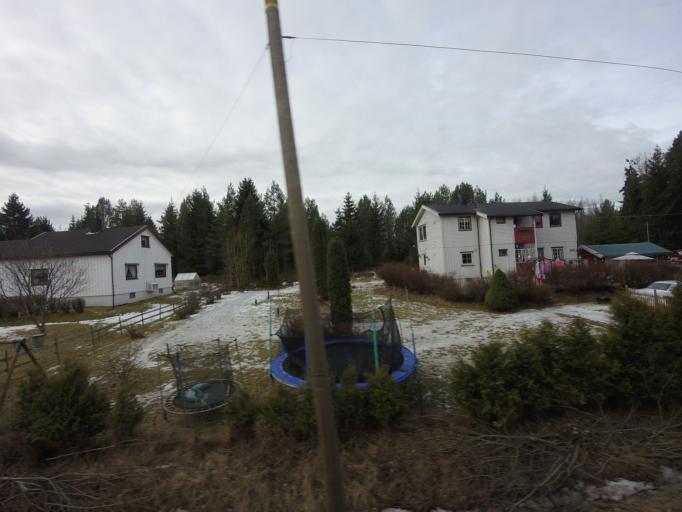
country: NO
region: Akershus
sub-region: Fet
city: Fetsund
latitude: 59.8991
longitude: 11.1887
